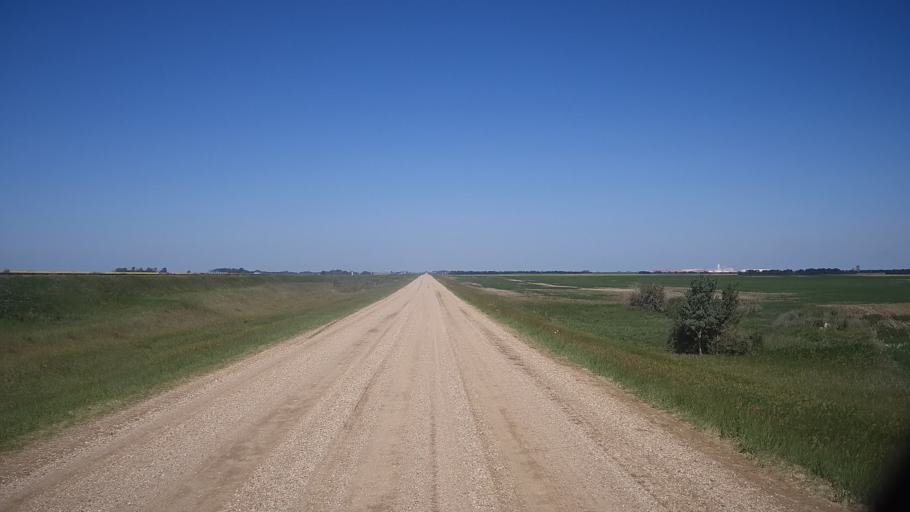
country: CA
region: Saskatchewan
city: Watrous
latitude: 51.8681
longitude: -105.9852
